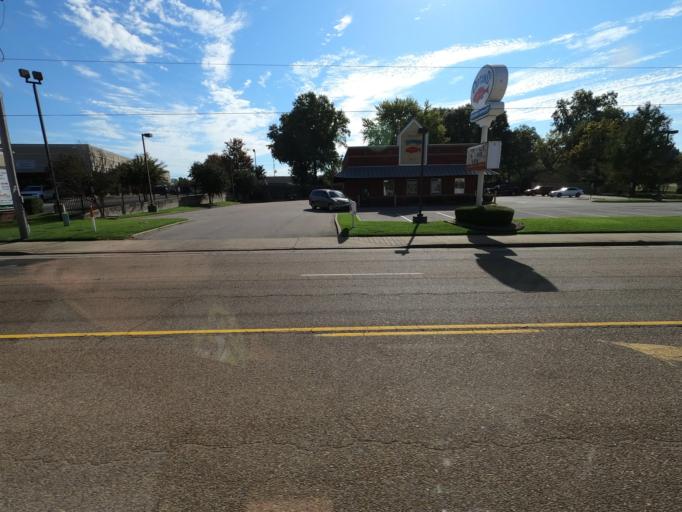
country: US
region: Tennessee
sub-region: Shelby County
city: Millington
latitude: 35.3541
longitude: -89.8971
